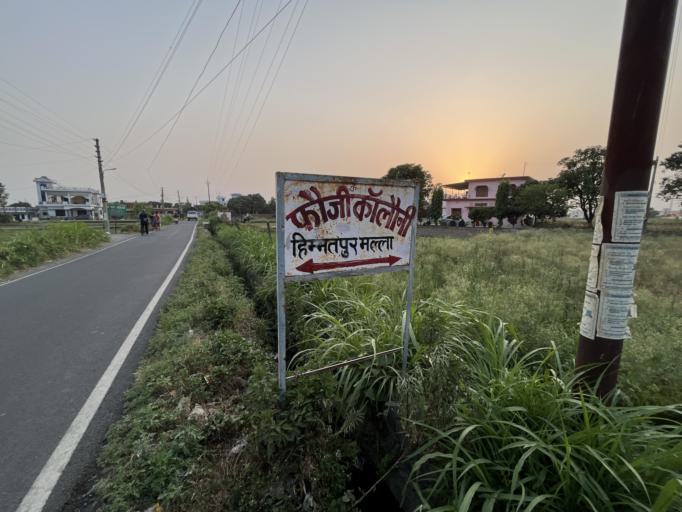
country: IN
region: Uttarakhand
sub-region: Naini Tal
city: Haldwani
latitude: 29.2204
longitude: 79.4879
